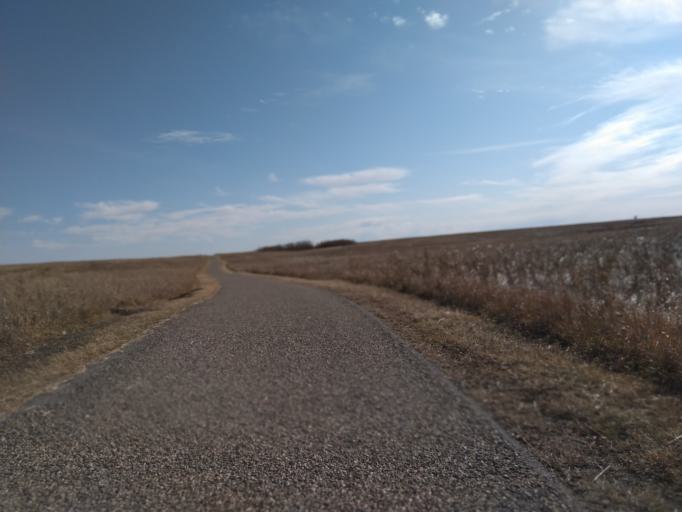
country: CA
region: Alberta
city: Calgary
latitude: 51.1224
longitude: -114.1248
